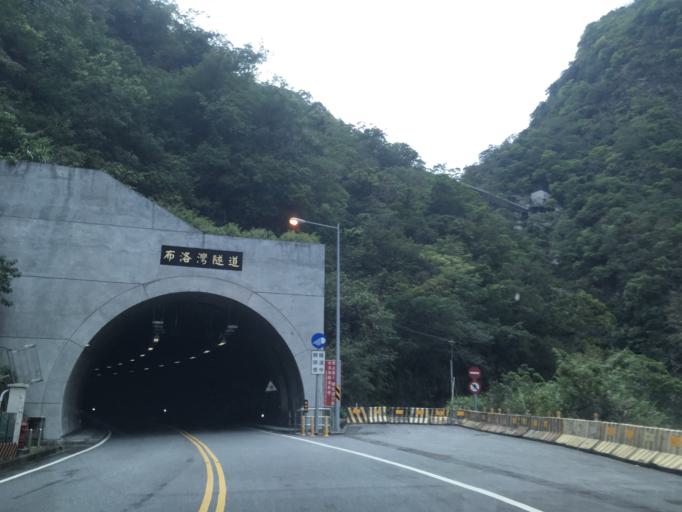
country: TW
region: Taiwan
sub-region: Hualien
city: Hualian
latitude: 24.1729
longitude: 121.5721
